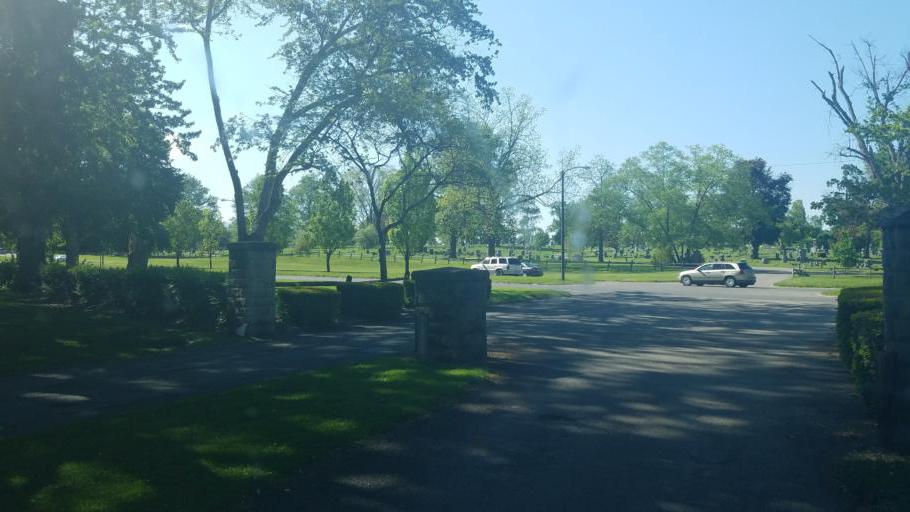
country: US
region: Ohio
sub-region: Marion County
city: Marion
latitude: 40.5739
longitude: -83.1208
